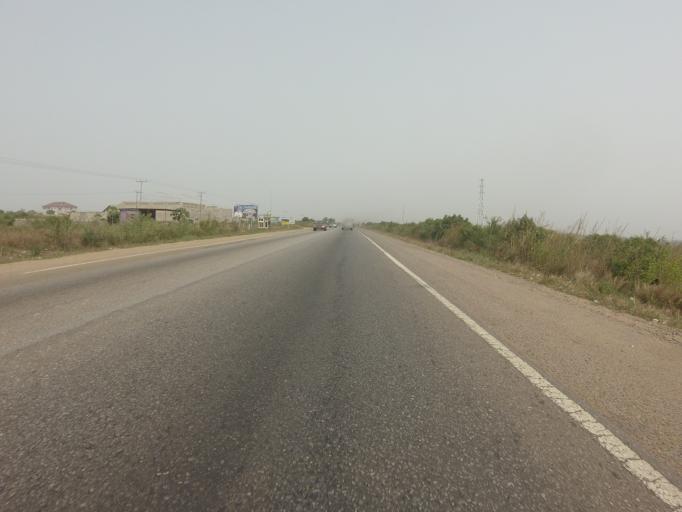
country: GH
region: Greater Accra
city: Tema
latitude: 5.7786
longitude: 0.0883
